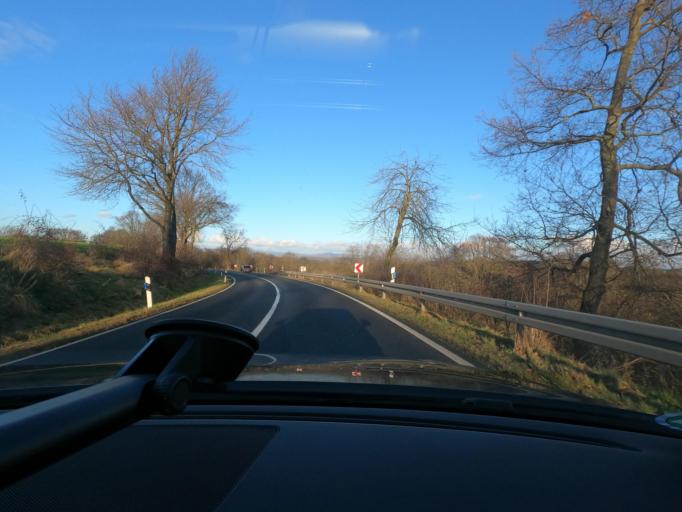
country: DE
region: Lower Saxony
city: Duderstadt
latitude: 51.5393
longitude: 10.2935
